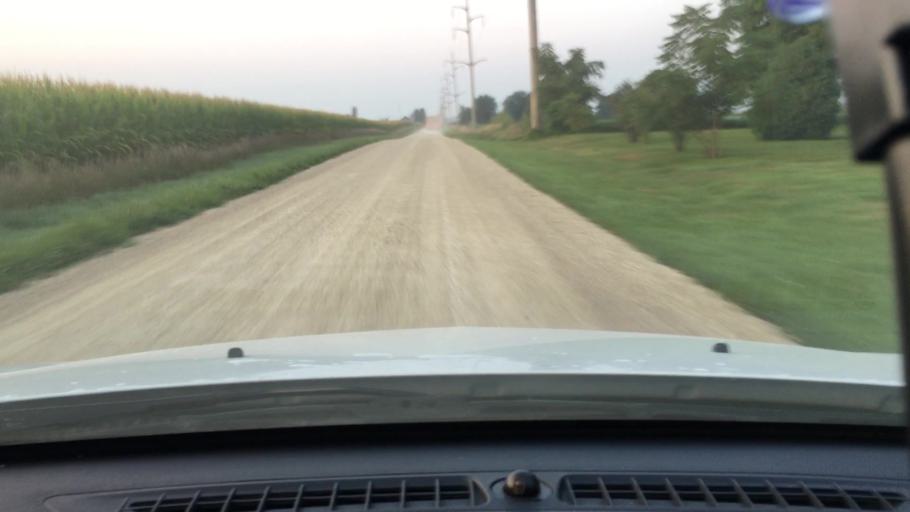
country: US
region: Illinois
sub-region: DeKalb County
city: Malta
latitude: 41.8621
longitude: -88.8280
